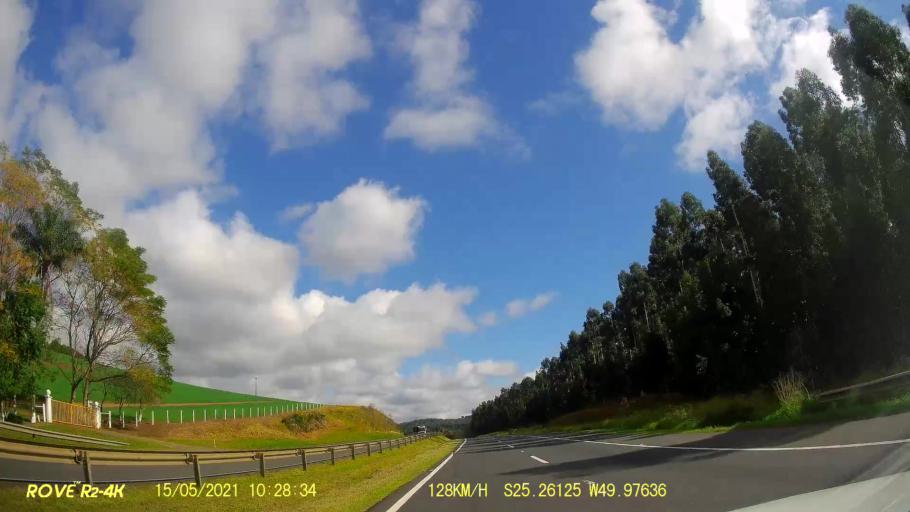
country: BR
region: Parana
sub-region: Palmeira
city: Palmeira
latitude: -25.2611
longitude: -49.9764
